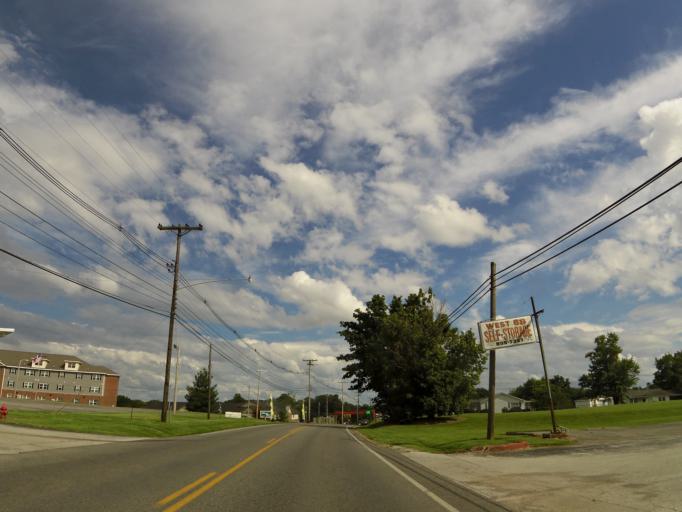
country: US
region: Kentucky
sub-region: Christian County
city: Hopkinsville
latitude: 36.8757
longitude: -87.5042
